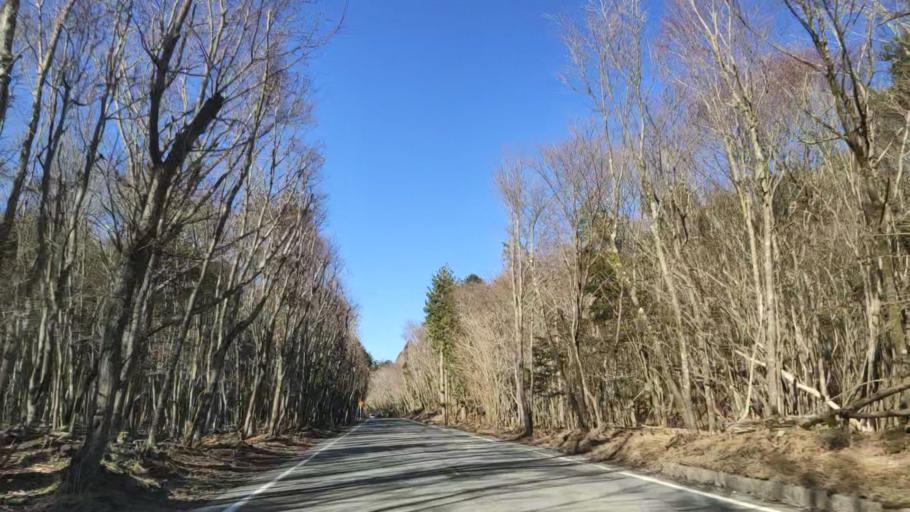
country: JP
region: Yamanashi
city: Fujikawaguchiko
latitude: 35.4469
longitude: 138.6409
